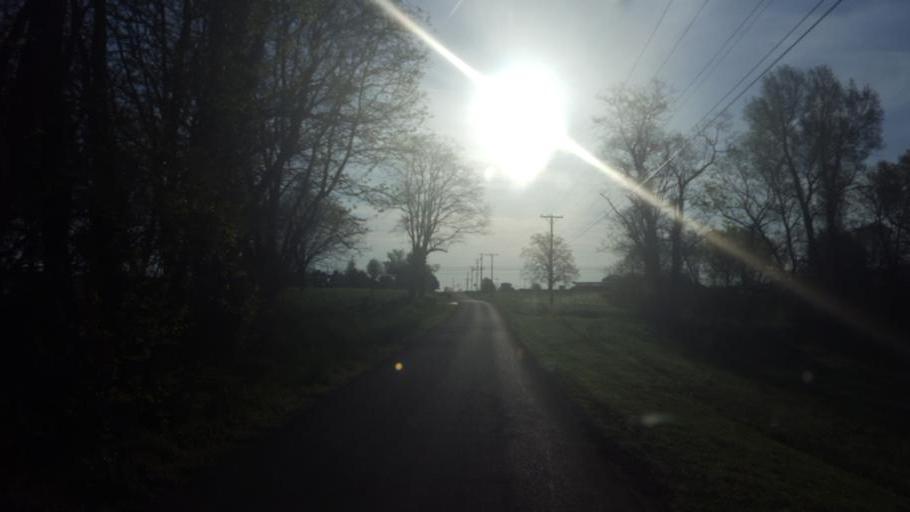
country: US
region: Kentucky
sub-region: Hart County
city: Munfordville
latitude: 37.2606
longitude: -85.8854
